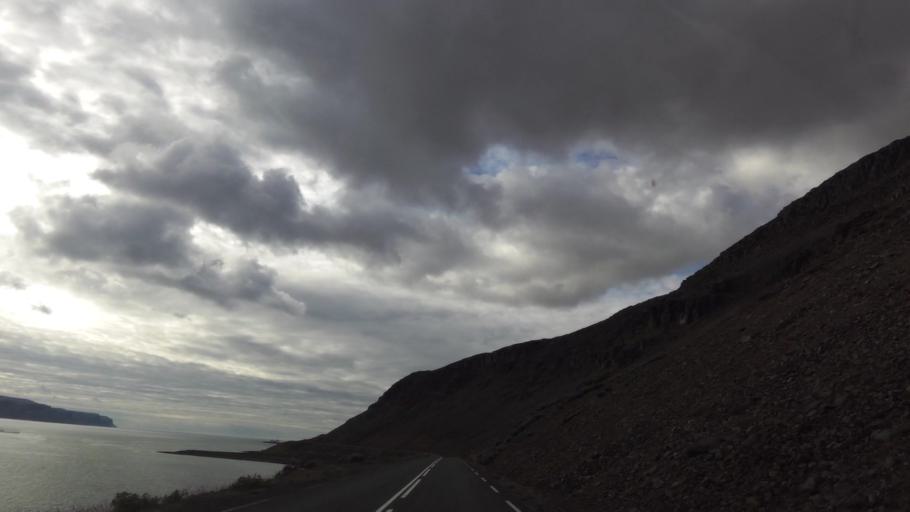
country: IS
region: West
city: Olafsvik
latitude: 65.5759
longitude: -23.9435
